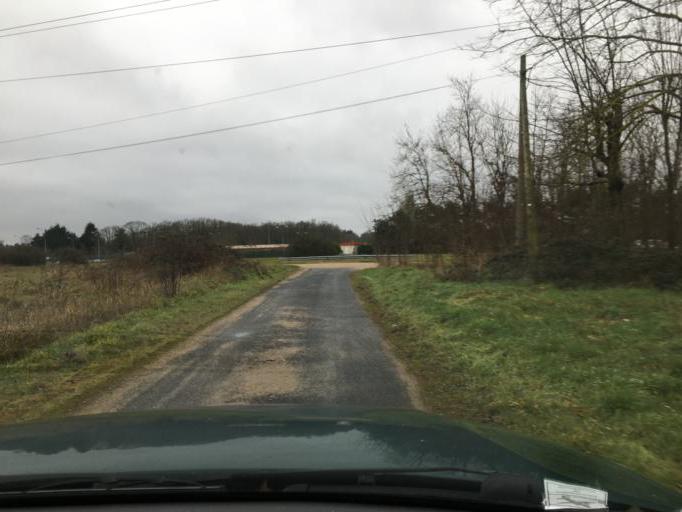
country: FR
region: Centre
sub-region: Departement du Loiret
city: Olivet
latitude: 47.8419
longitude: 1.8844
